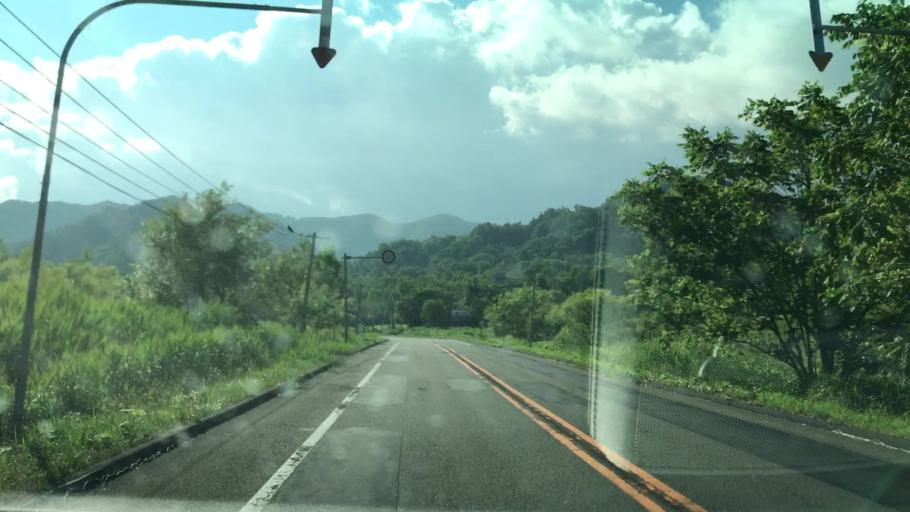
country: JP
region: Hokkaido
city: Shimo-furano
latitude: 42.8973
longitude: 142.4269
